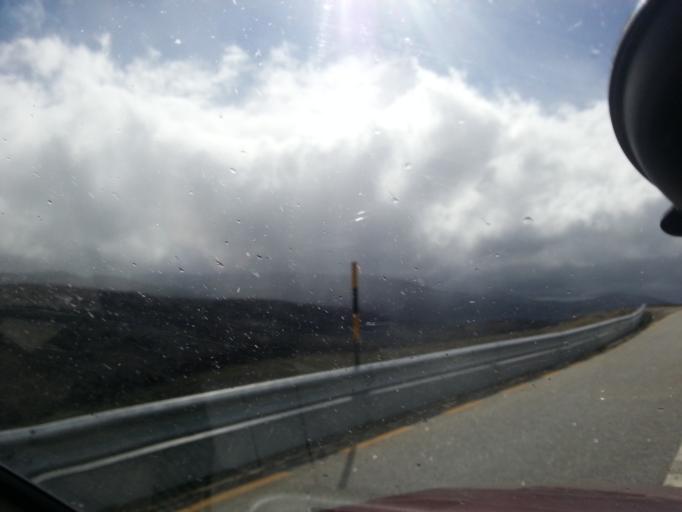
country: PT
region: Guarda
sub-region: Manteigas
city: Manteigas
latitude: 40.4190
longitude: -7.6079
